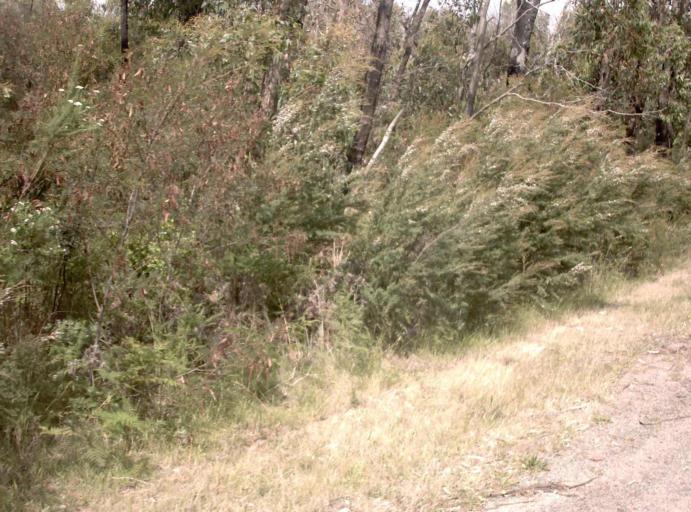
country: AU
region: Victoria
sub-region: Latrobe
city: Traralgon
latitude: -38.3099
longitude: 146.5596
